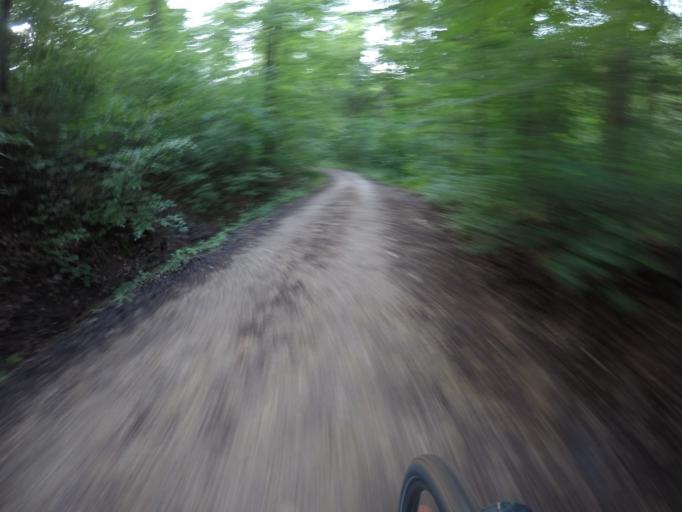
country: DE
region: Baden-Wuerttemberg
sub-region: Regierungsbezirk Stuttgart
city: Schlaitdorf
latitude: 48.6160
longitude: 9.2134
